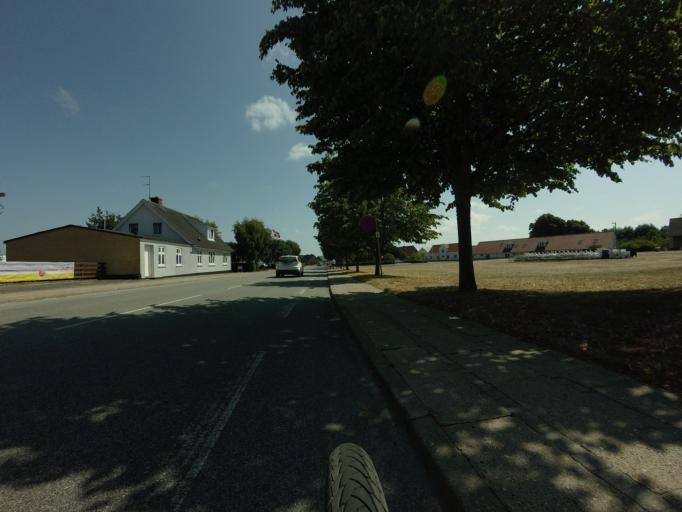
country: DK
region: North Denmark
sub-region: Laeso Kommune
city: Byrum
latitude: 57.2552
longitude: 11.0009
